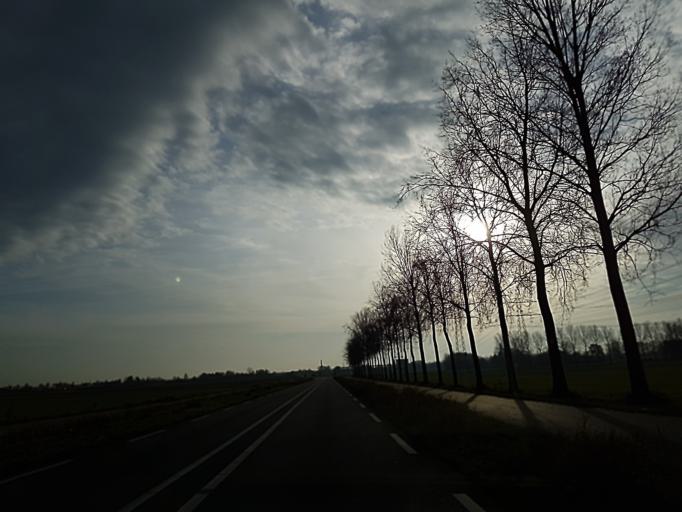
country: NL
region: North Brabant
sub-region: Roosendaal
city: Roosendaal
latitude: 51.5550
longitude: 4.4884
